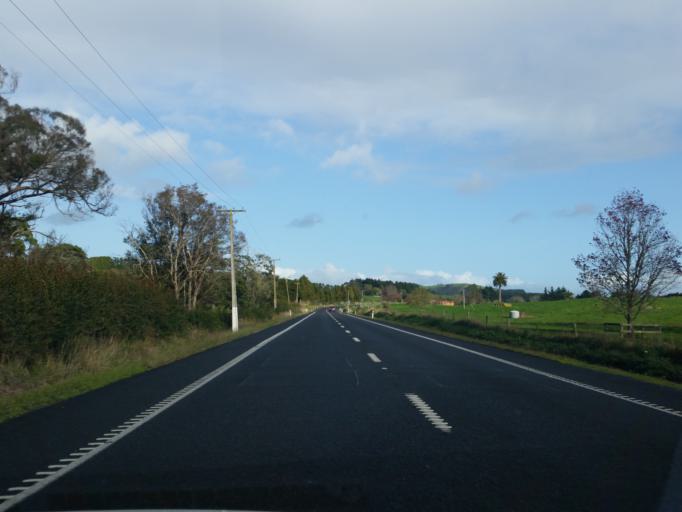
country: NZ
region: Waikato
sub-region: Hauraki District
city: Ngatea
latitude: -37.2880
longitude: 175.3881
